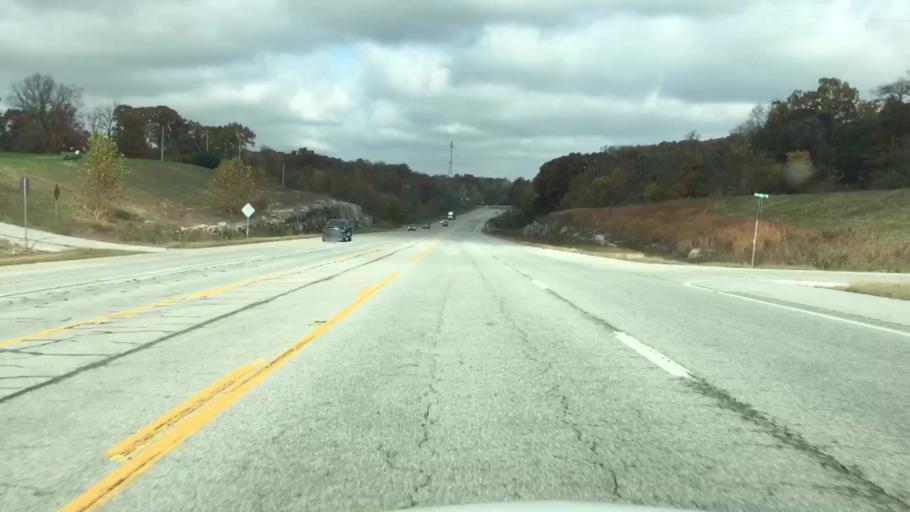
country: US
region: Arkansas
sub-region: Benton County
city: Gentry
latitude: 36.2385
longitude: -94.4875
